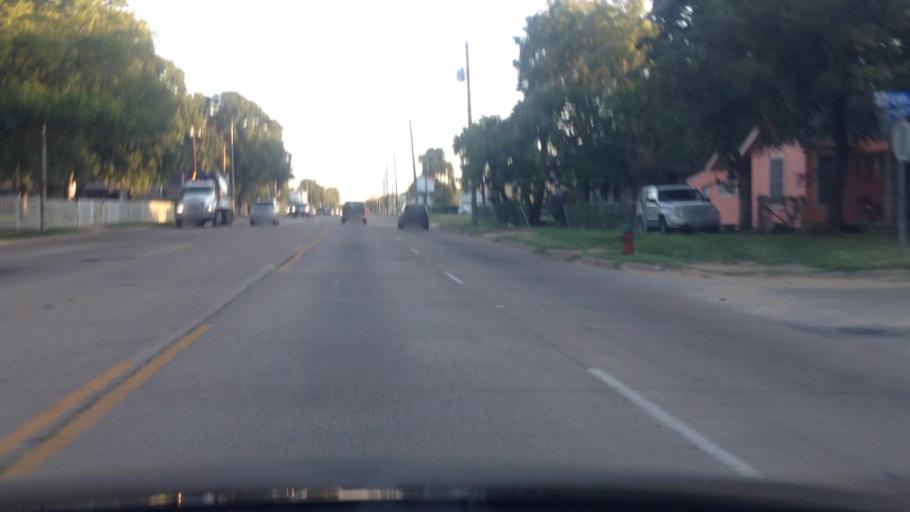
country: US
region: Texas
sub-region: Tarrant County
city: Haltom City
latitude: 32.7863
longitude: -97.2906
